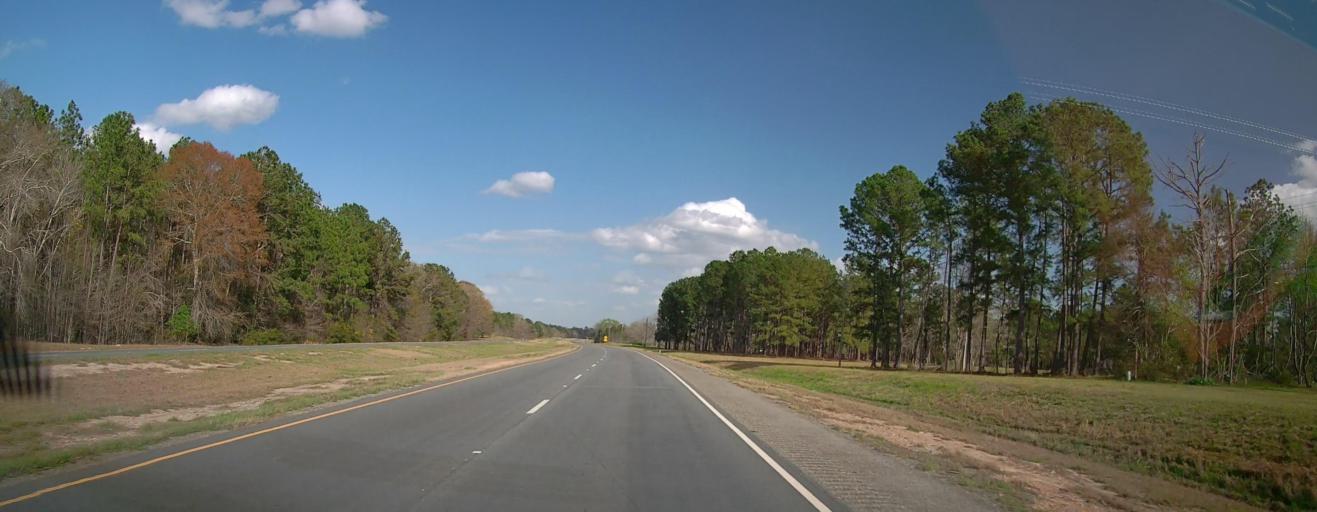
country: US
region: Georgia
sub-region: Telfair County
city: Helena
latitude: 32.1039
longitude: -82.9943
